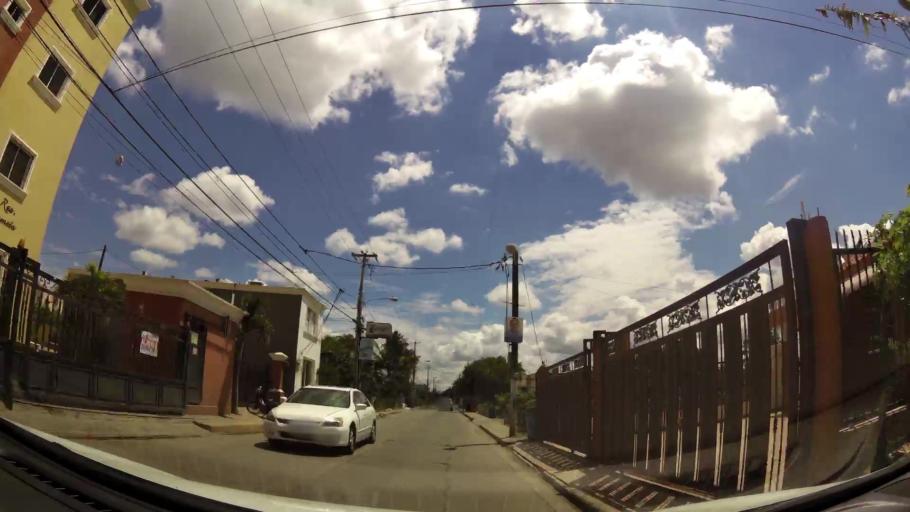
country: DO
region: Santiago
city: Santiago de los Caballeros
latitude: 19.4750
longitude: -70.6682
